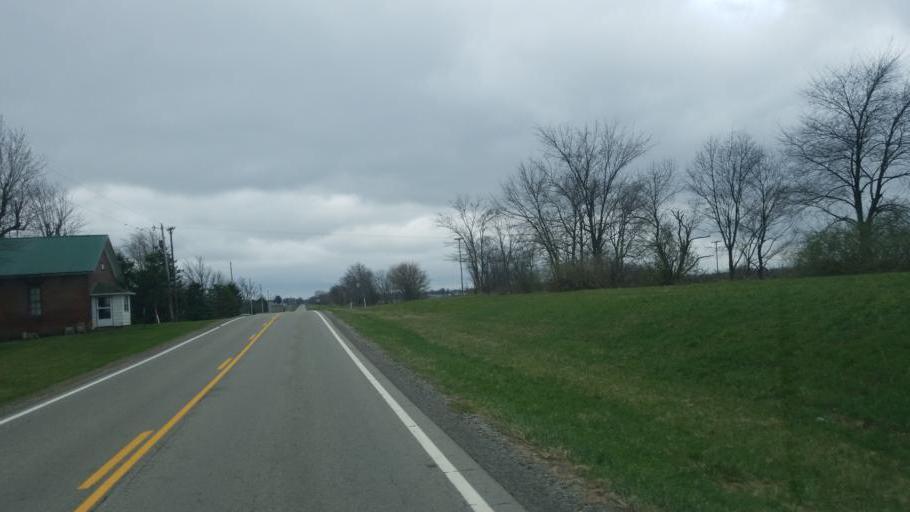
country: US
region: Ohio
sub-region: Hardin County
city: Kenton
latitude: 40.6747
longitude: -83.5953
